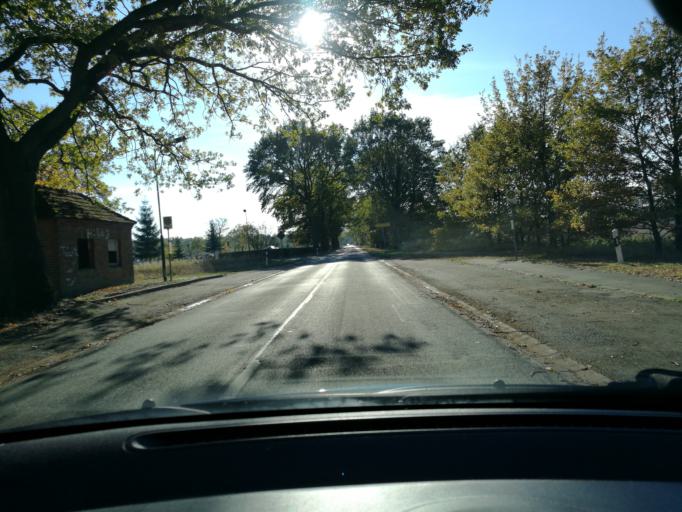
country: DE
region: Mecklenburg-Vorpommern
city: Neu Kaliss
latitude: 53.1376
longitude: 11.3209
